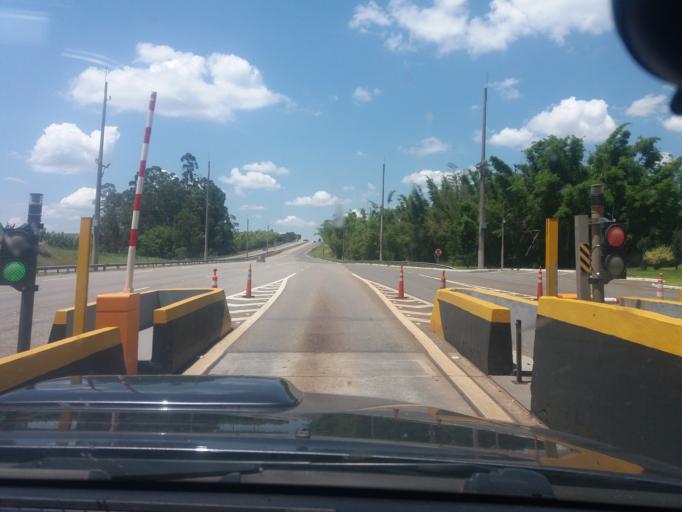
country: BR
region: Sao Paulo
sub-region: Itapetininga
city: Itapetininga
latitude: -23.4710
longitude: -47.9682
